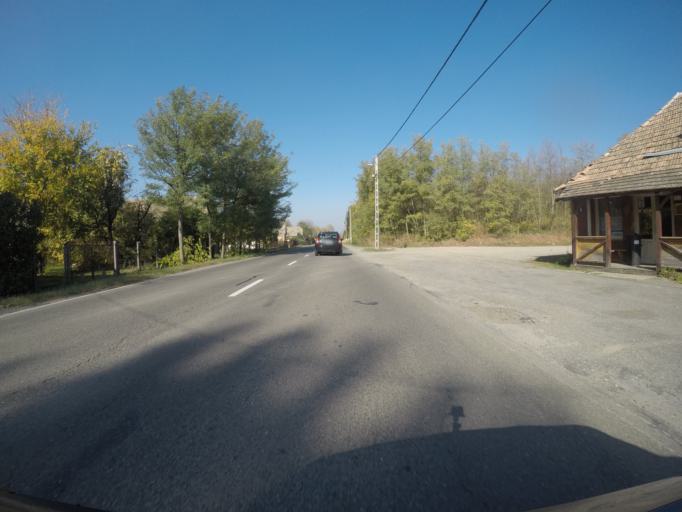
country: HU
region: Tolna
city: Szedres
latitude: 46.5092
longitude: 18.6663
